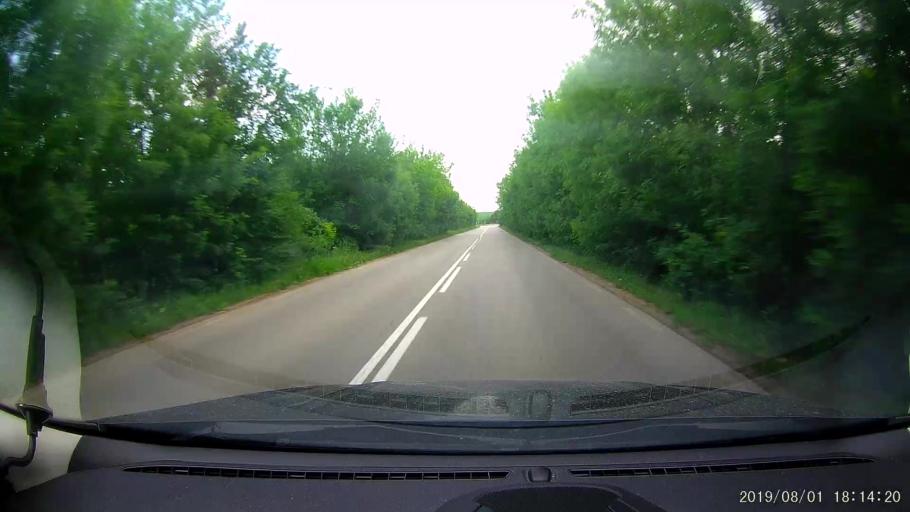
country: BG
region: Silistra
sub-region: Obshtina Dulovo
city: Dulovo
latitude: 43.7710
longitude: 27.1260
